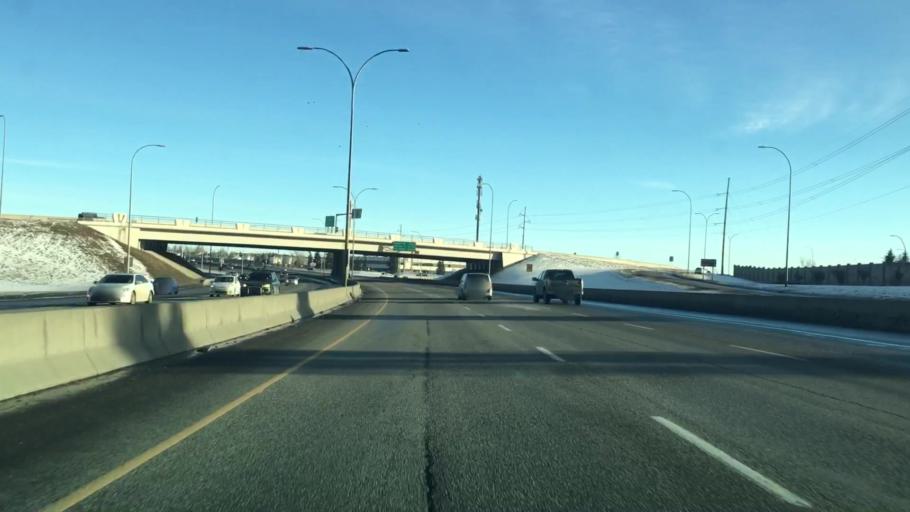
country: CA
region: Alberta
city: Calgary
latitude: 50.9815
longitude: -114.0179
